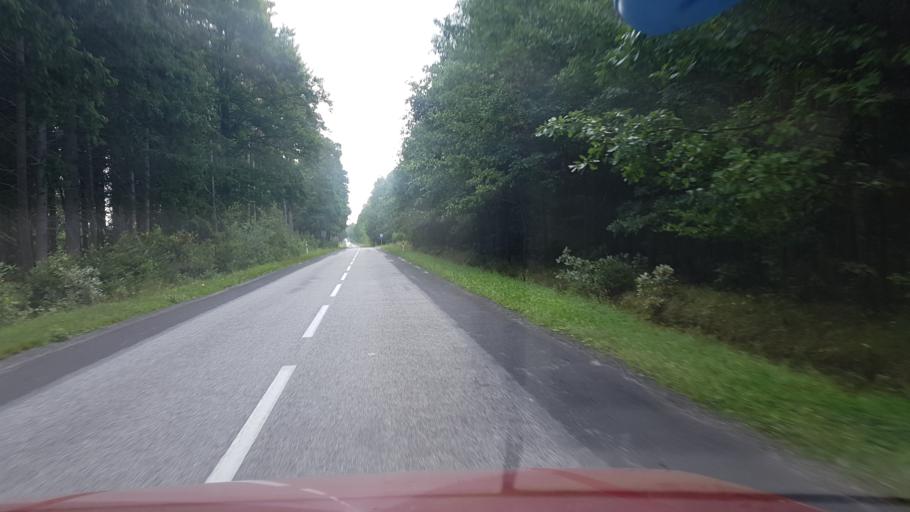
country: PL
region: West Pomeranian Voivodeship
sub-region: Powiat koszalinski
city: Polanow
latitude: 54.1008
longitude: 16.8114
